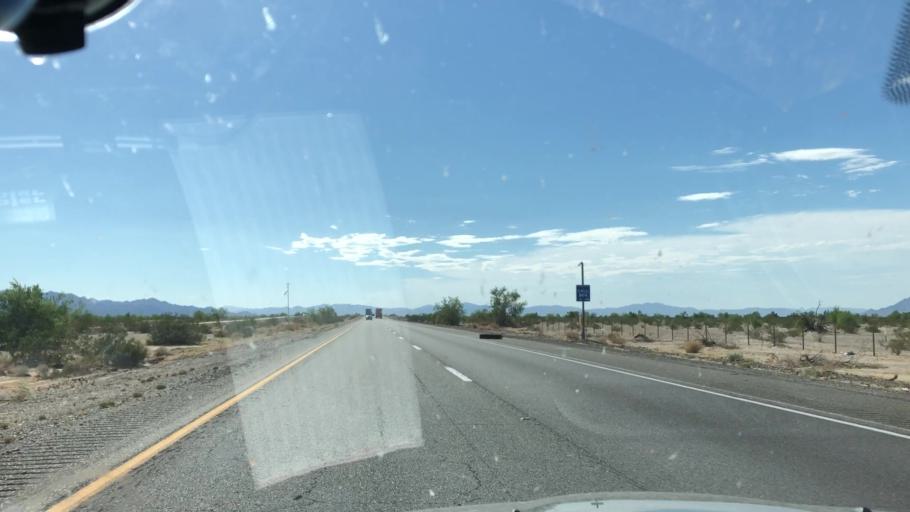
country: US
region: California
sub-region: Riverside County
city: Mesa Verde
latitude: 33.6551
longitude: -115.1514
